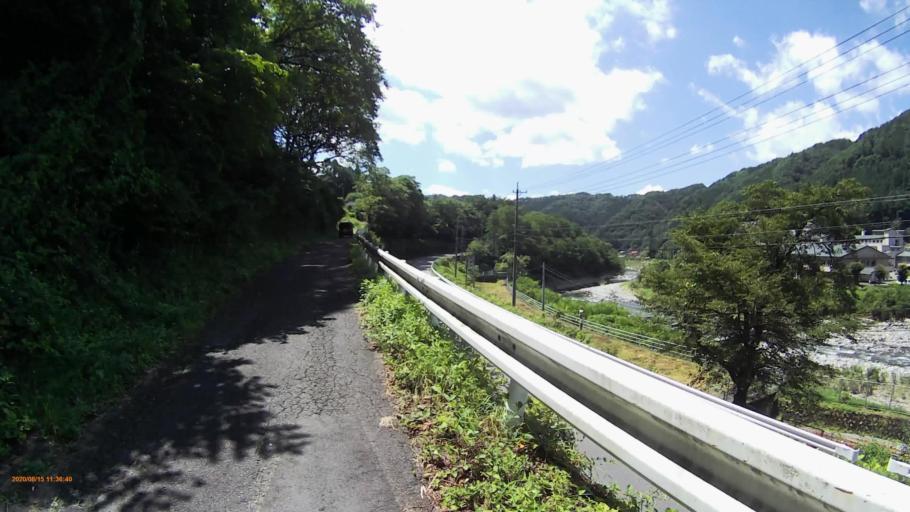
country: JP
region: Nagano
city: Ina
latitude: 35.8357
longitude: 137.6868
